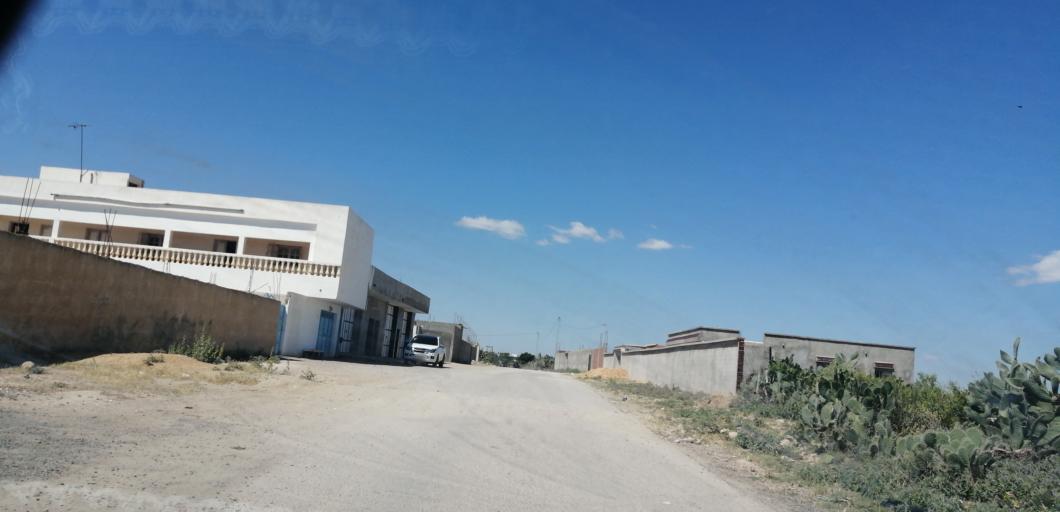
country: TN
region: Al Qayrawan
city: Kairouan
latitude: 35.6257
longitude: 9.9283
